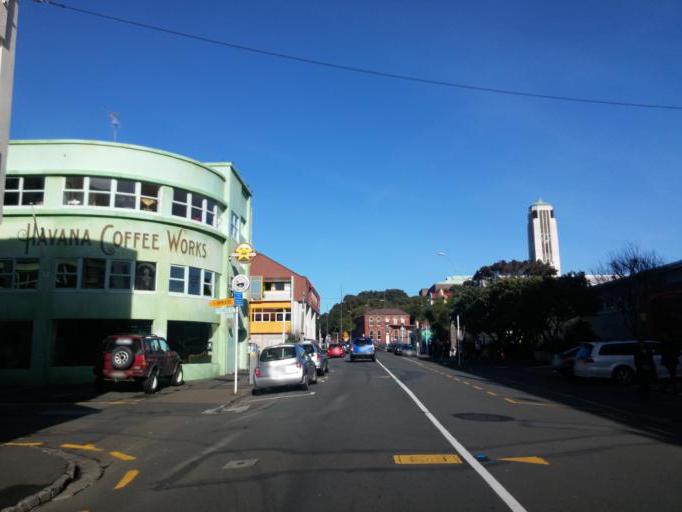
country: NZ
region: Wellington
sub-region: Wellington City
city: Wellington
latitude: -41.2974
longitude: 174.7790
